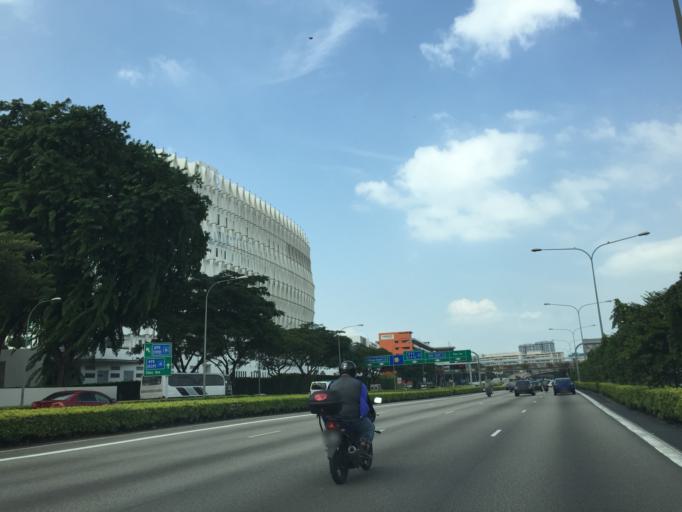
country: SG
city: Singapore
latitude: 1.3247
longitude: 103.8719
